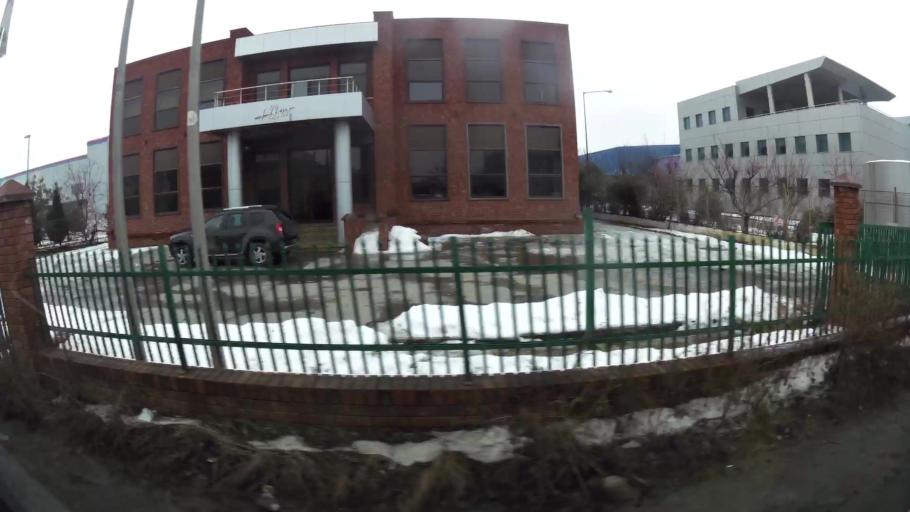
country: RO
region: Ilfov
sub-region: Comuna Chiajna
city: Chiajna
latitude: 44.4384
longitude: 25.9874
